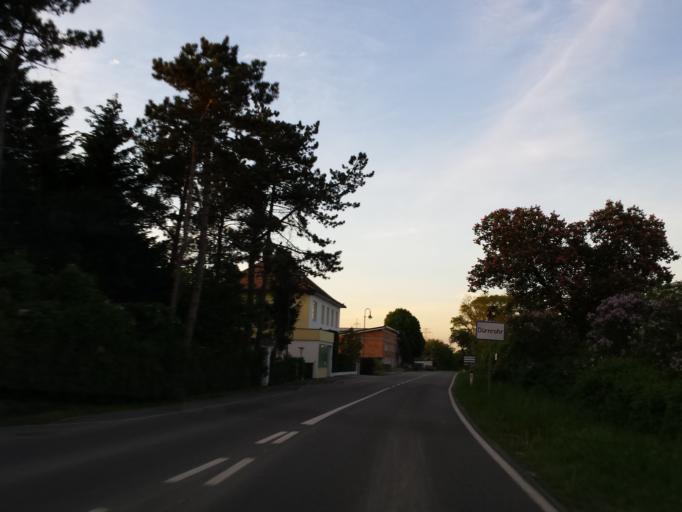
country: AT
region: Lower Austria
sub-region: Politischer Bezirk Tulln
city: Atzenbrugg
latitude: 48.3209
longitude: 15.9056
